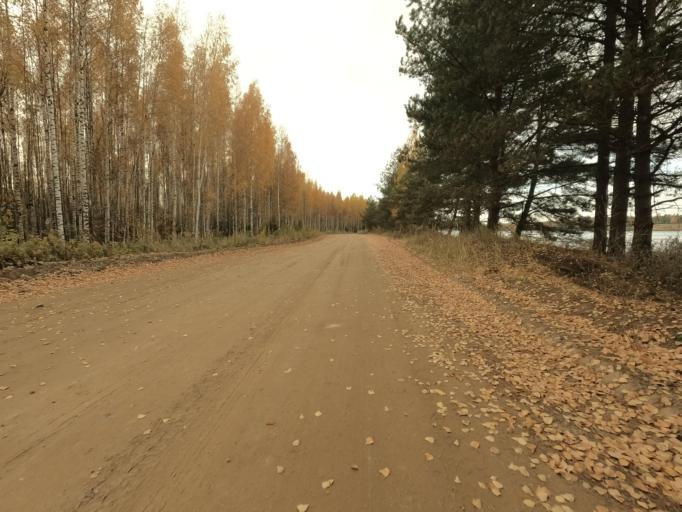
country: RU
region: Leningrad
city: Priladozhskiy
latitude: 59.7116
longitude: 31.3560
